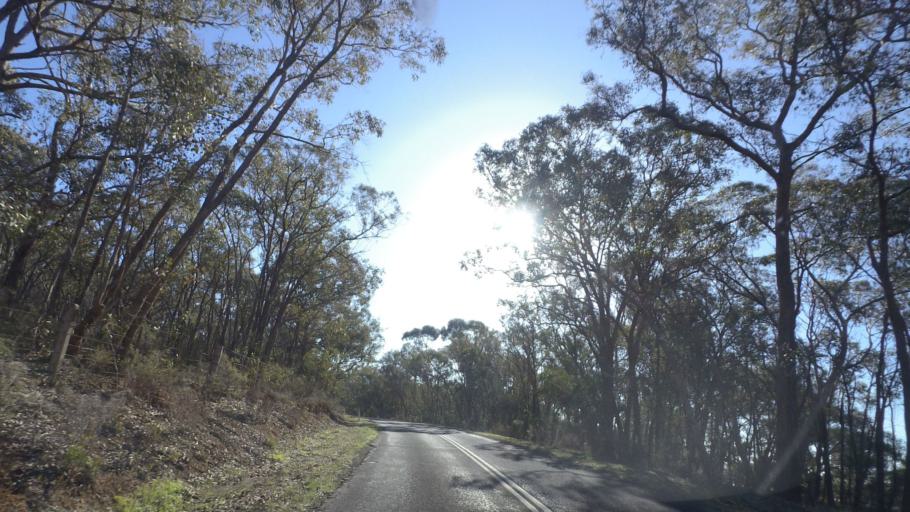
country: AU
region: Victoria
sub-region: Greater Bendigo
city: Kangaroo Flat
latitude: -36.8857
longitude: 144.2861
